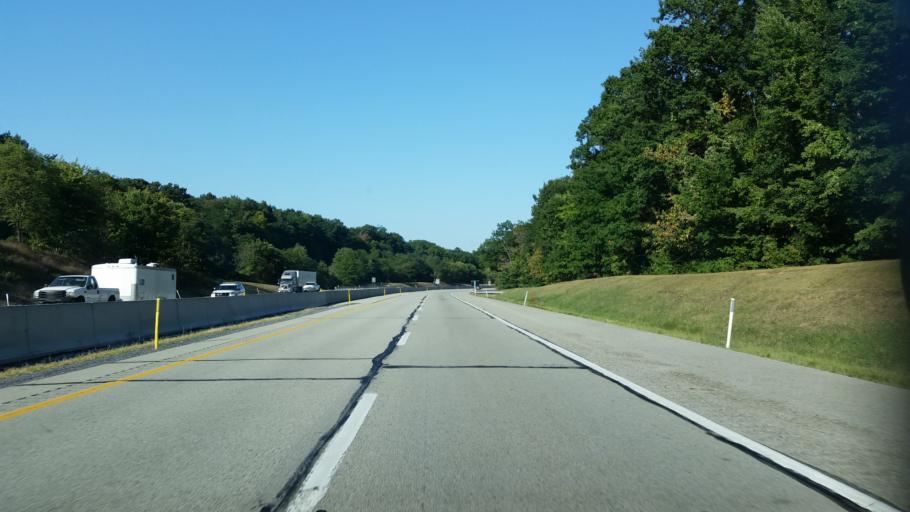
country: US
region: Pennsylvania
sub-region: Fulton County
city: McConnellsburg
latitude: 40.0568
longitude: -78.0976
